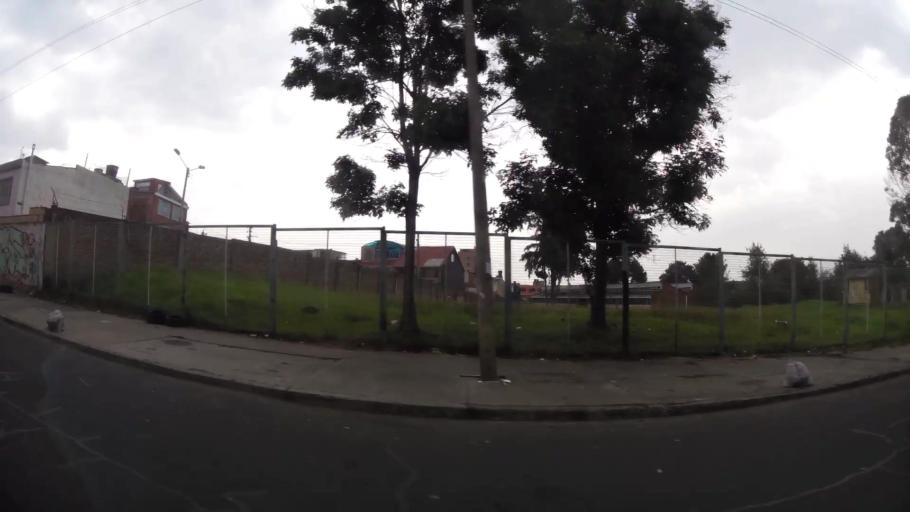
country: CO
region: Bogota D.C.
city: Bogota
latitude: 4.5783
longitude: -74.0901
